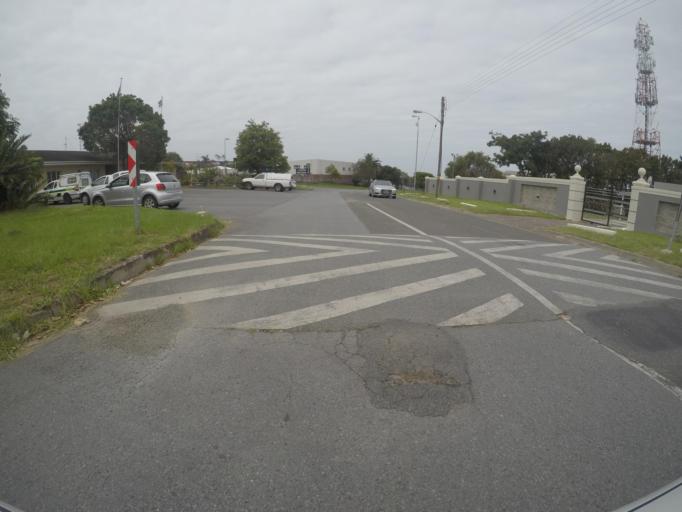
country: ZA
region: Eastern Cape
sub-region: Buffalo City Metropolitan Municipality
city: East London
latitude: -32.9692
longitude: 27.9385
